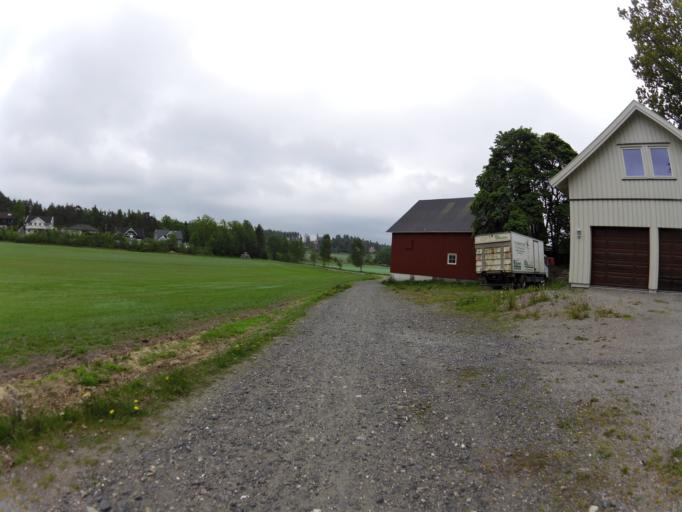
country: NO
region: Ostfold
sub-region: Moss
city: Moss
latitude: 59.3852
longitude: 10.6822
